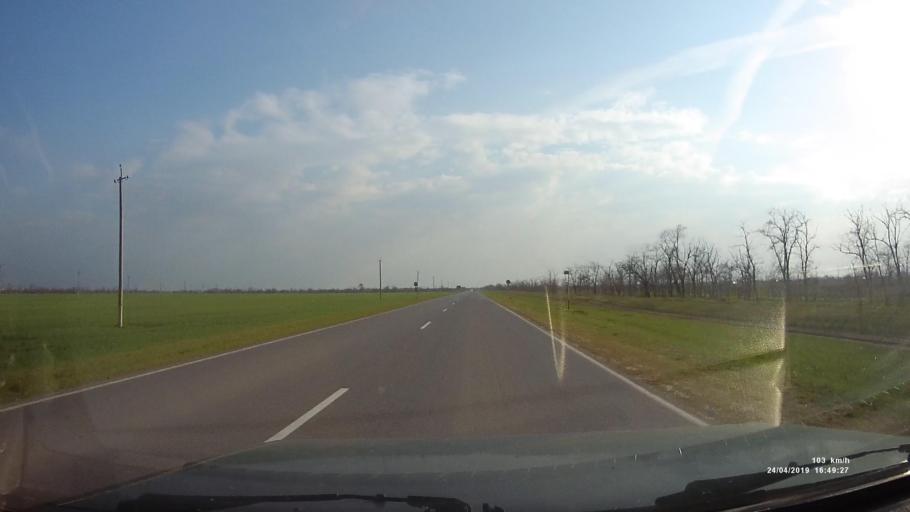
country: RU
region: Rostov
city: Proletarsk
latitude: 46.7172
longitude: 41.7639
